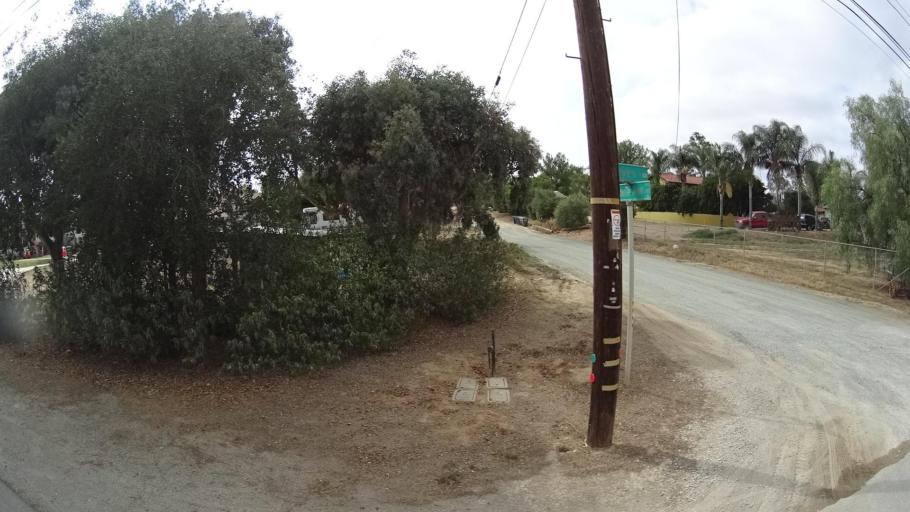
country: US
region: California
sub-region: San Diego County
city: Ramona
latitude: 33.0304
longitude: -116.8493
